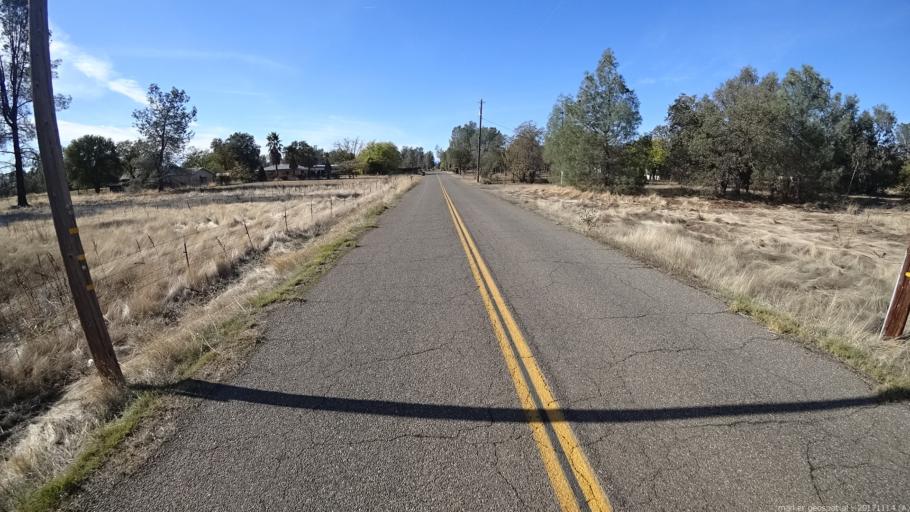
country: US
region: California
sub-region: Shasta County
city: Anderson
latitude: 40.4321
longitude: -122.4140
